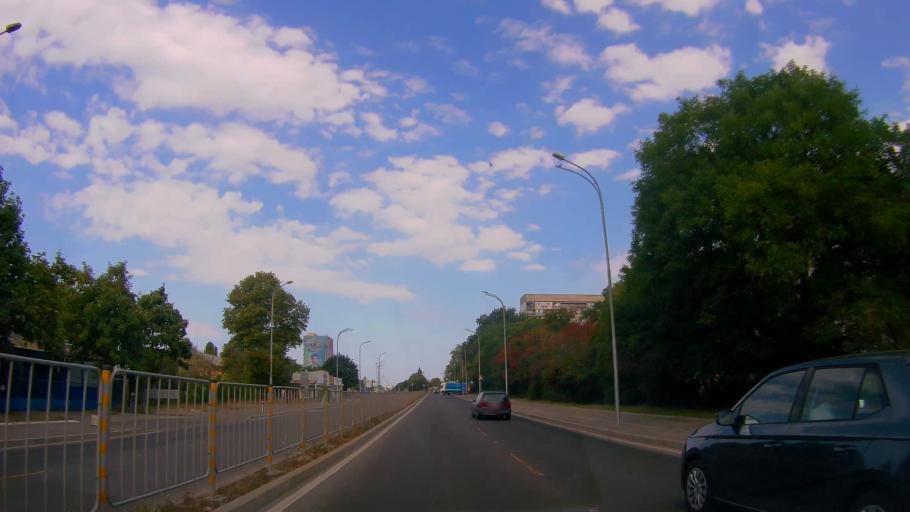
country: BG
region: Burgas
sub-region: Obshtina Burgas
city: Burgas
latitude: 42.5185
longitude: 27.4443
